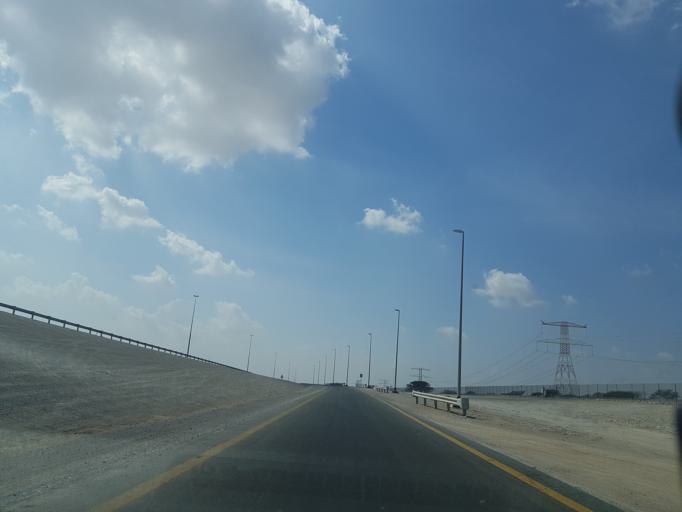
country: AE
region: Ra's al Khaymah
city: Ras al-Khaimah
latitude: 25.7624
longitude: 56.0215
